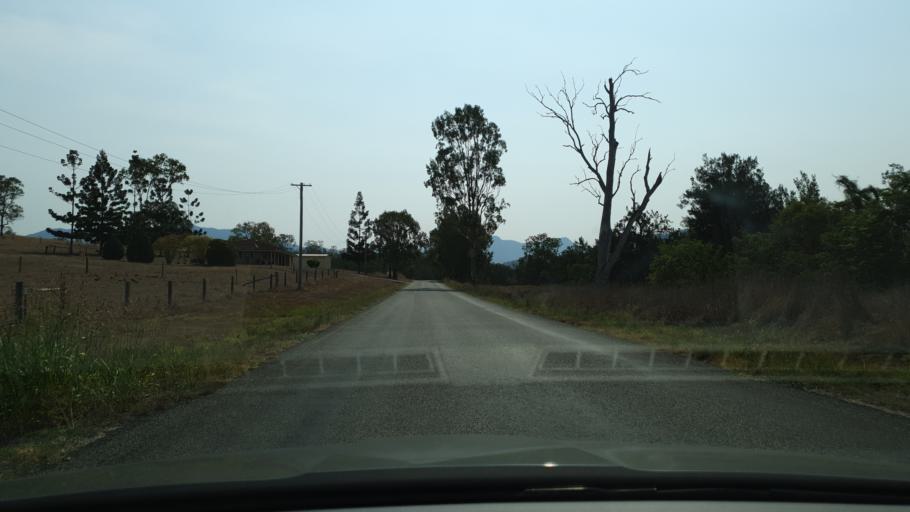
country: AU
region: Queensland
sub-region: Ipswich
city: Deebing Heights
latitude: -28.1374
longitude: 152.5915
